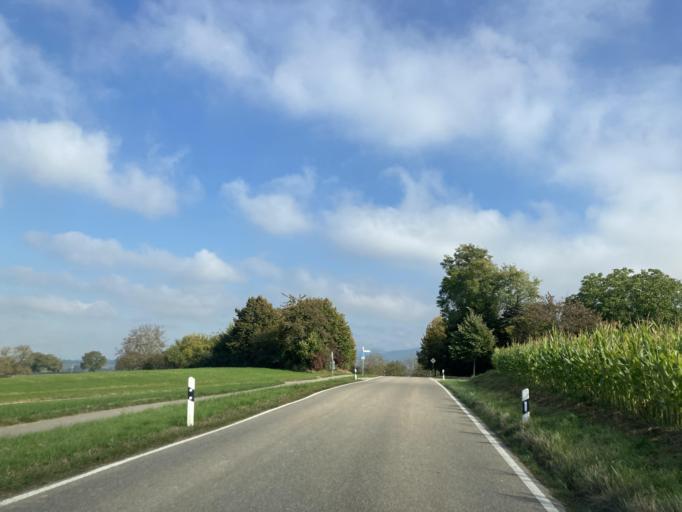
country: DE
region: Baden-Wuerttemberg
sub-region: Freiburg Region
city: Mullheim
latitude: 47.8147
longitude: 7.6425
